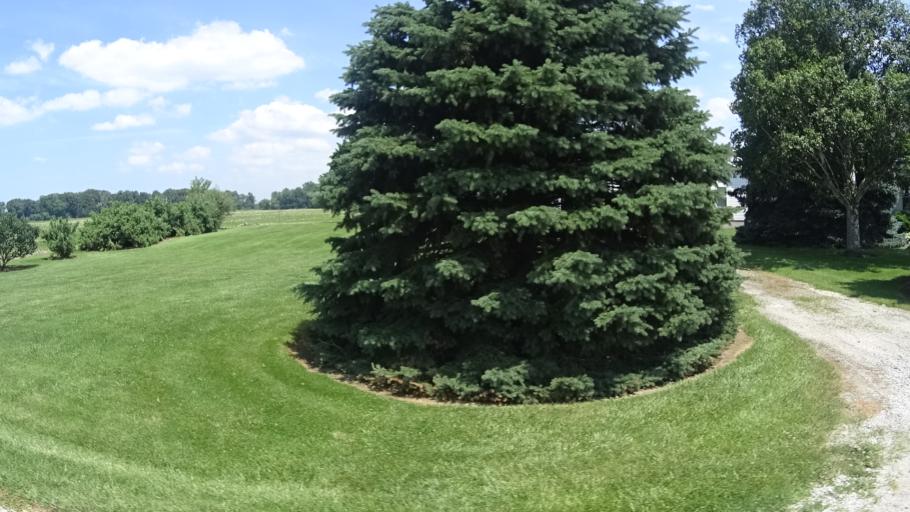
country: US
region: Ohio
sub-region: Erie County
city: Huron
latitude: 41.3525
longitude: -82.5366
